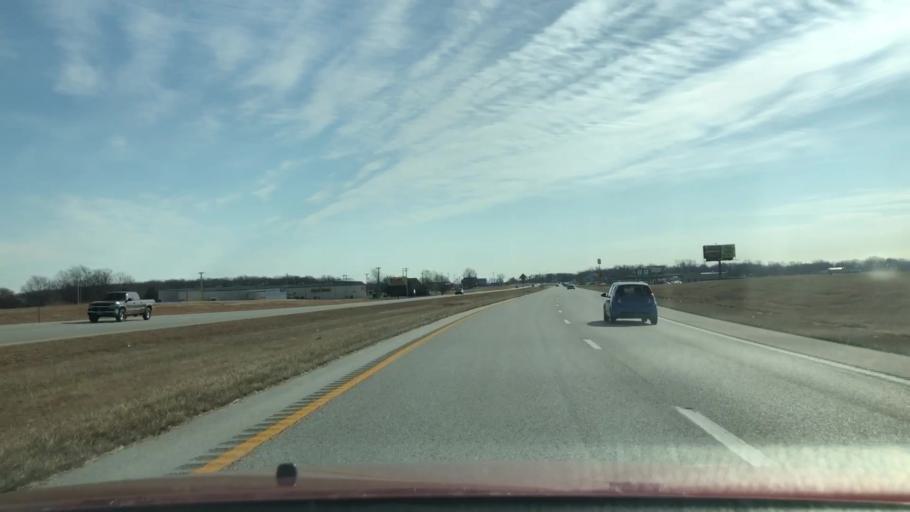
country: US
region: Missouri
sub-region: Webster County
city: Seymour
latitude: 37.1538
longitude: -92.7577
